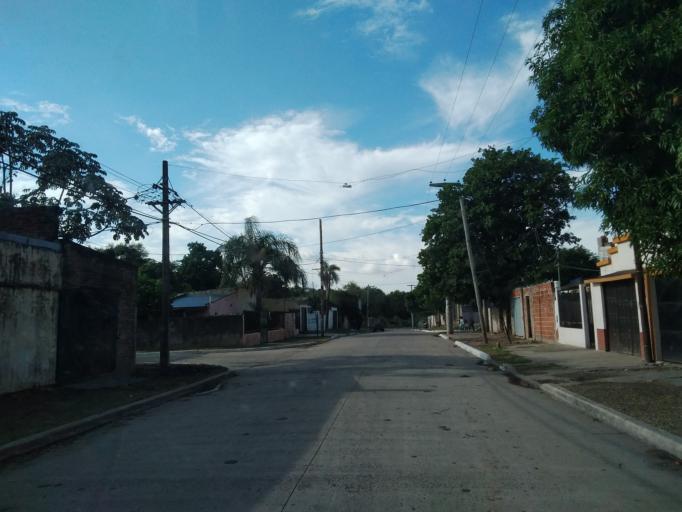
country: AR
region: Corrientes
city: Corrientes
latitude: -27.4632
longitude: -58.8137
